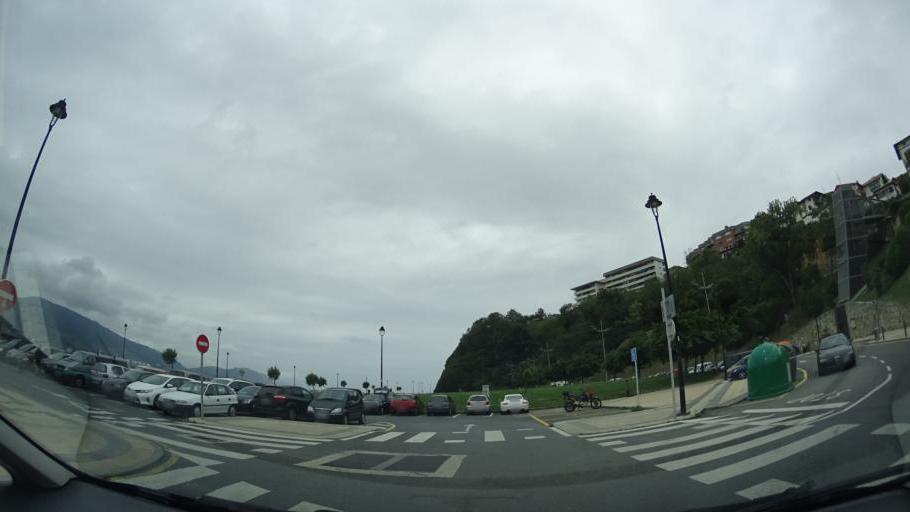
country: ES
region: Basque Country
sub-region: Bizkaia
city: Algorta
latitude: 43.3493
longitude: -3.0152
